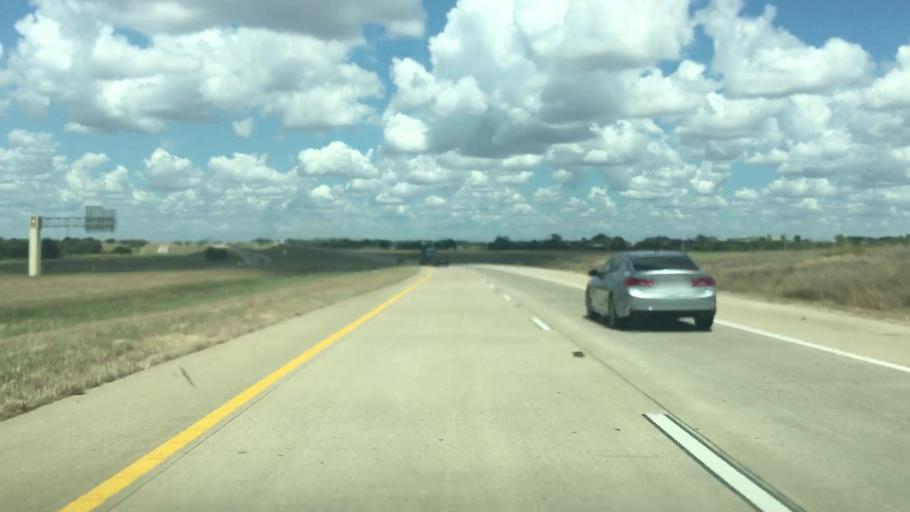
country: US
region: Texas
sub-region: Williamson County
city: Hutto
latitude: 30.5541
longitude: -97.5767
